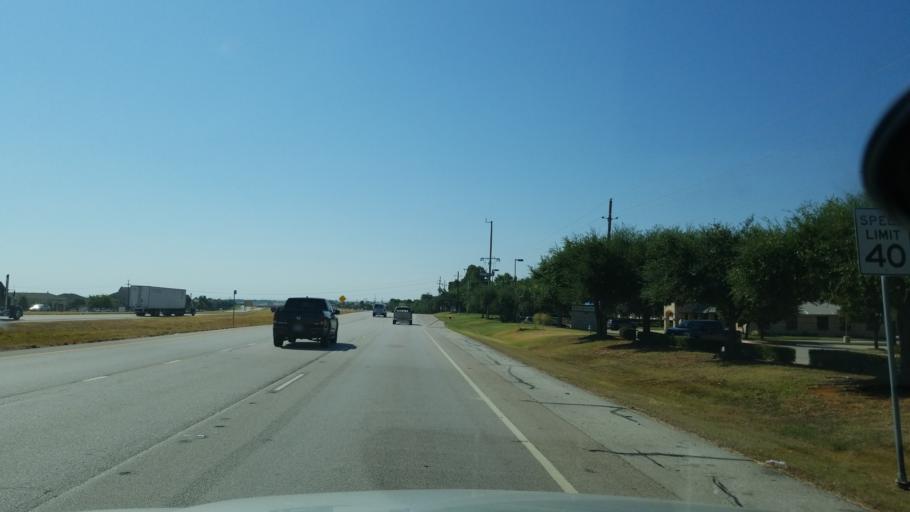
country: US
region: Texas
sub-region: Tarrant County
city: Mansfield
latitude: 32.5893
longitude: -97.1413
